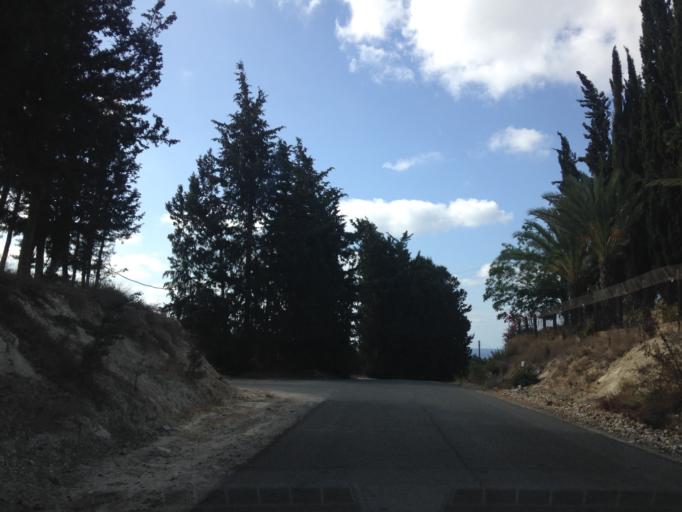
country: CY
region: Pafos
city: Pegeia
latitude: 34.8686
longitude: 32.3626
